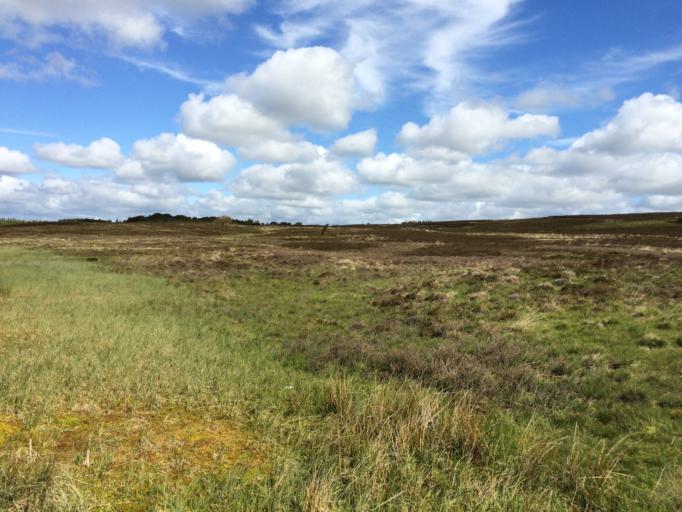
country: DK
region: Central Jutland
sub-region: Holstebro Kommune
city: Holstebro
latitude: 56.2284
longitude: 8.6173
